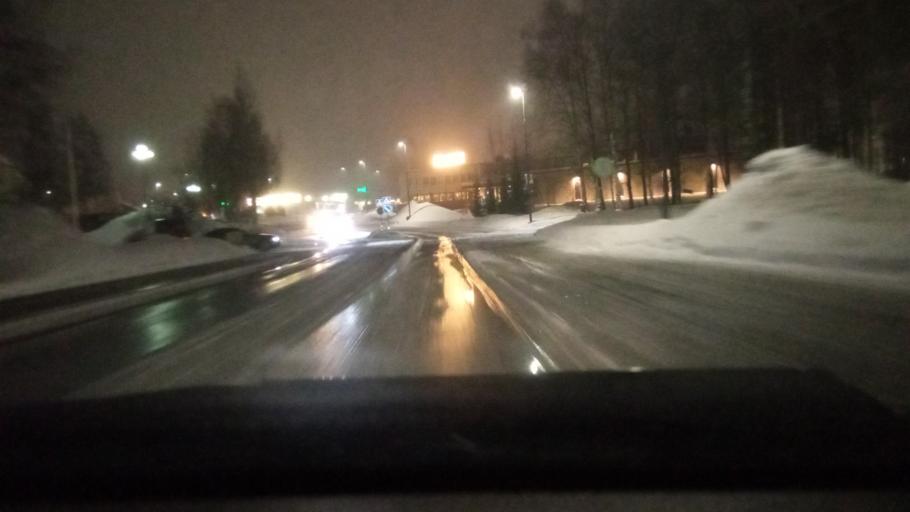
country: FI
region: Southern Ostrobothnia
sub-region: Jaerviseutu
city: Alajaervi
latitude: 63.0023
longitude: 23.8122
